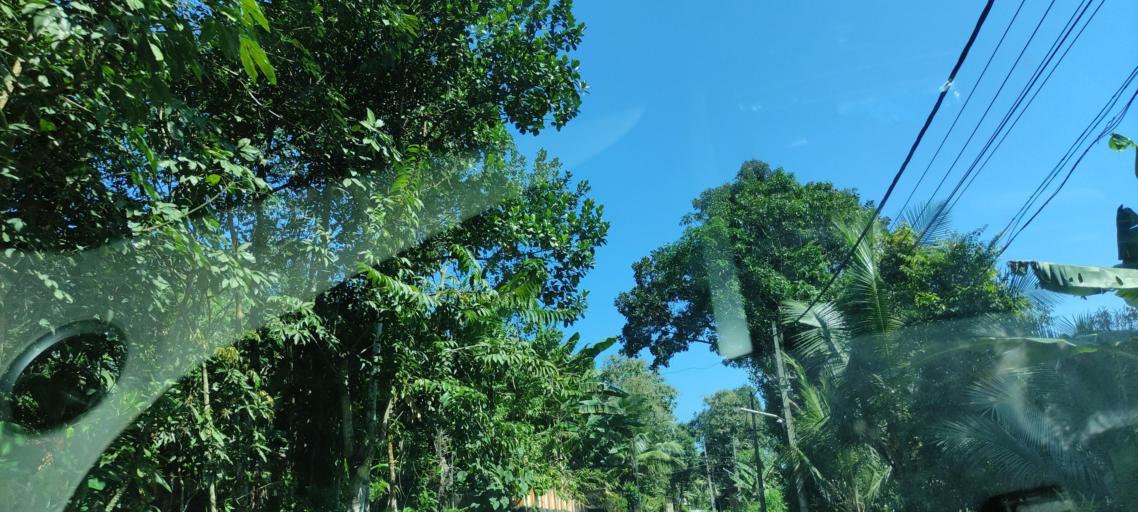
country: IN
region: Kerala
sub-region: Pattanamtitta
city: Adur
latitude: 9.0952
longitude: 76.7336
